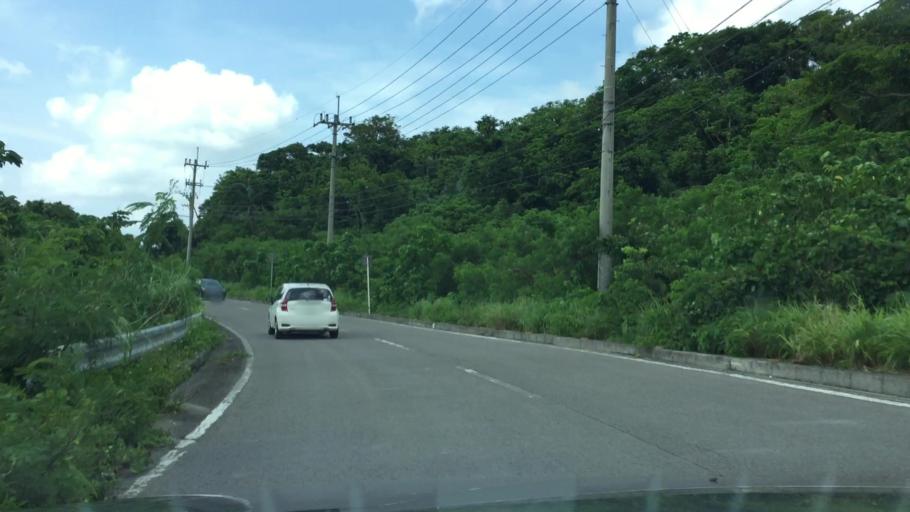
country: JP
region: Okinawa
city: Ishigaki
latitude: 24.4576
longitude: 124.2268
